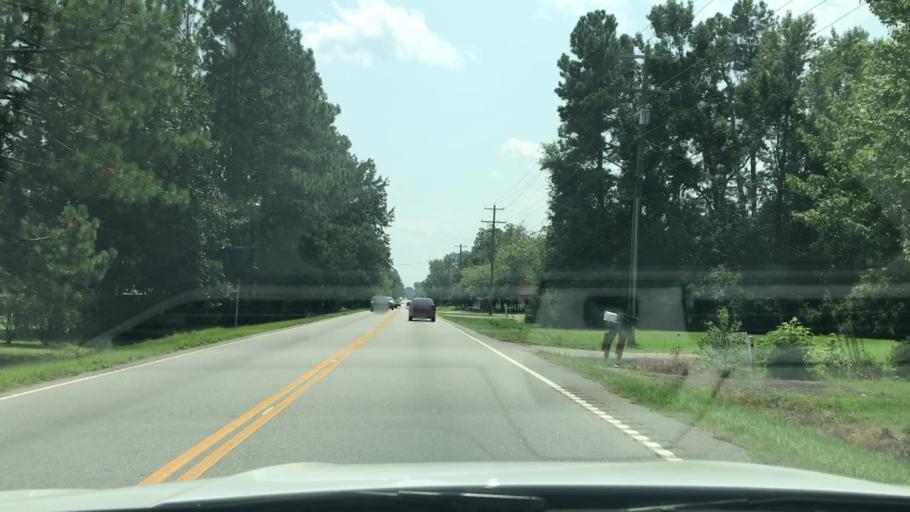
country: US
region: South Carolina
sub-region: Horry County
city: Conway
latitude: 33.8118
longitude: -79.0781
